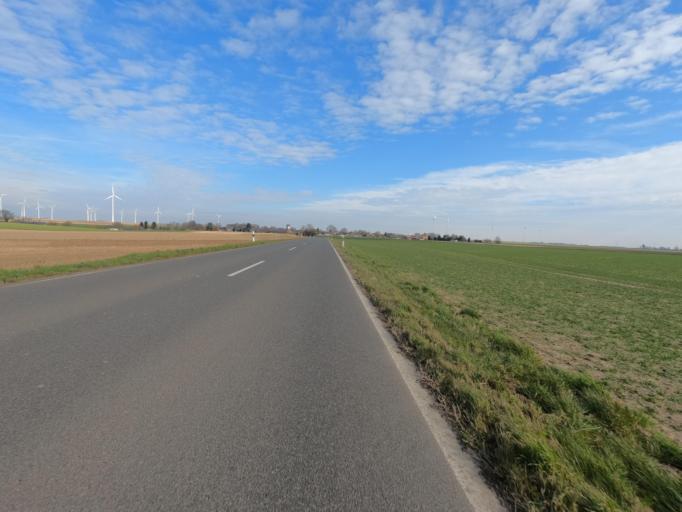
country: DE
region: North Rhine-Westphalia
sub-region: Regierungsbezirk Koln
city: Linnich
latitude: 50.9950
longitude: 6.3166
